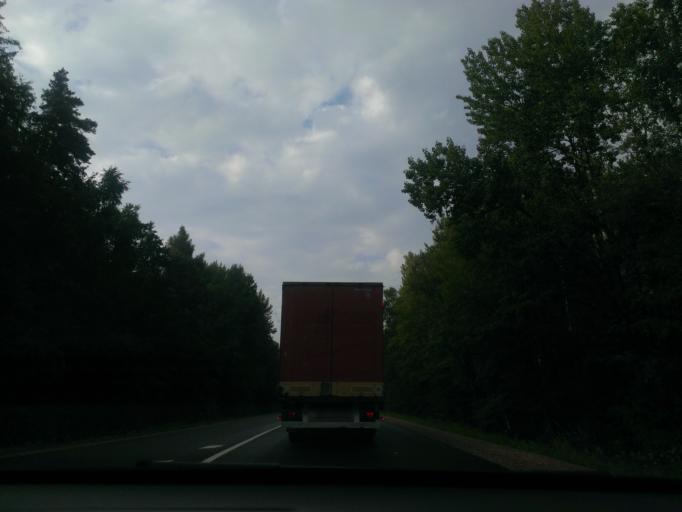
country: LV
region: Lecava
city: Iecava
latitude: 56.6630
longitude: 24.2330
